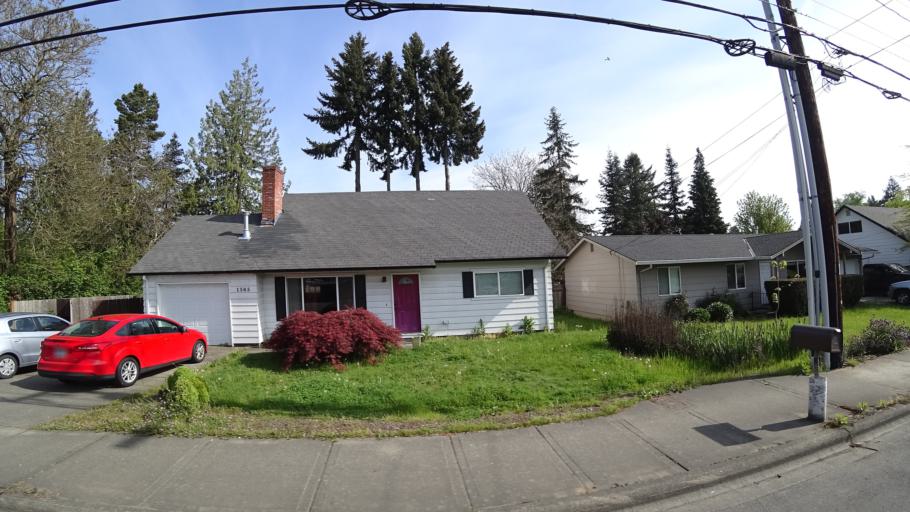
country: US
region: Oregon
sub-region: Washington County
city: Hillsboro
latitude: 45.5217
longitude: -122.9665
